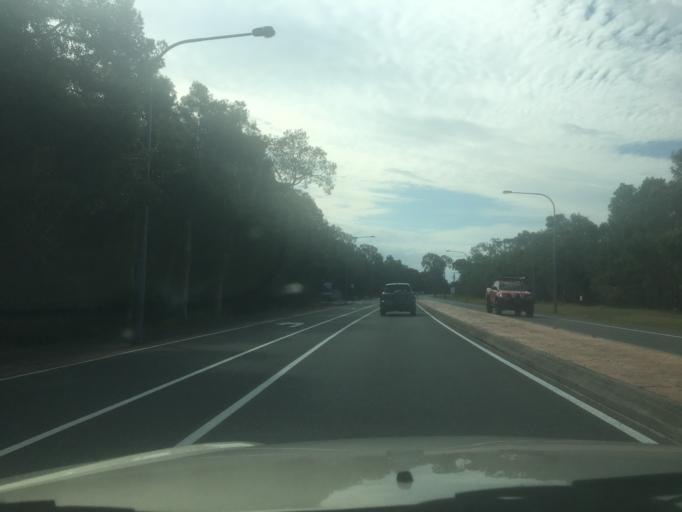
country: AU
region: Queensland
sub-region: Moreton Bay
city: Bongaree
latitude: -27.0800
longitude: 153.1677
